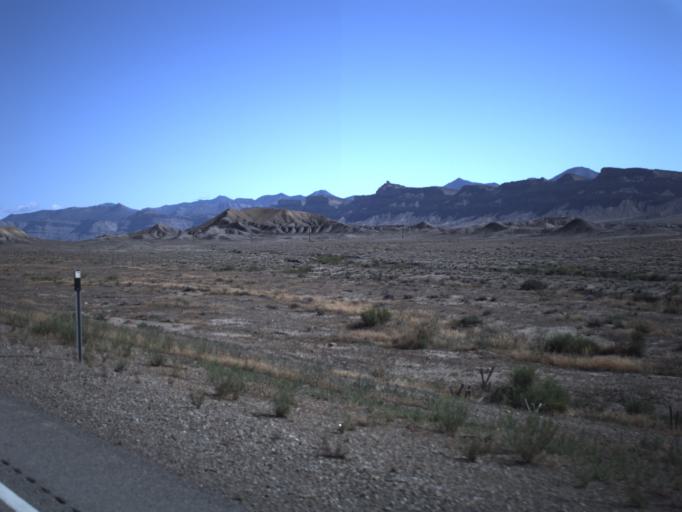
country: US
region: Utah
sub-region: Carbon County
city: East Carbon City
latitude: 39.2743
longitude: -110.3468
